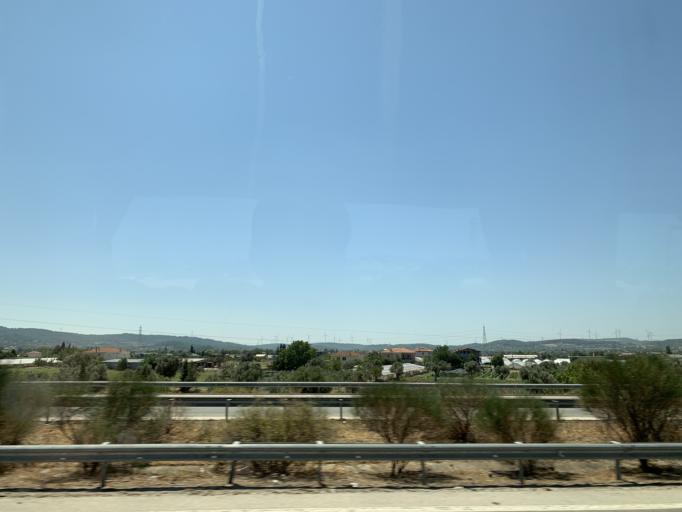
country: TR
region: Izmir
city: Urla
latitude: 38.2984
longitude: 26.7376
